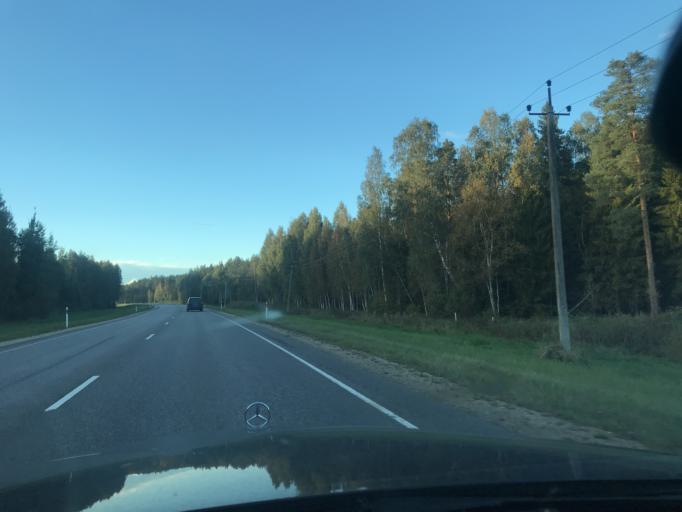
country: EE
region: Vorumaa
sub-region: Voru linn
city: Voru
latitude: 57.8335
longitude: 27.0611
